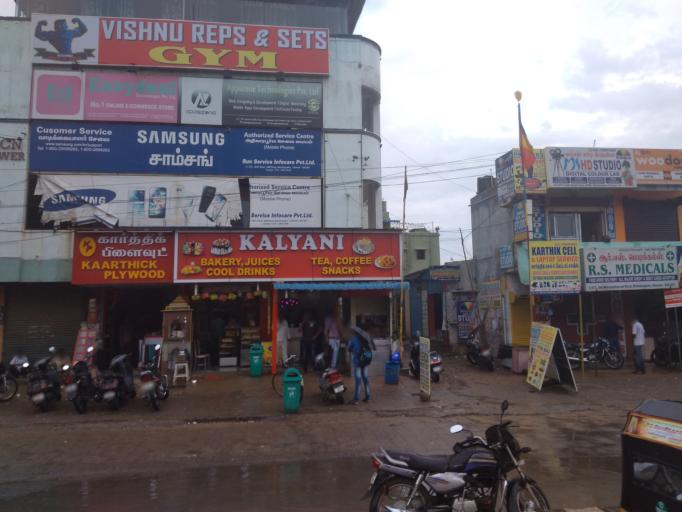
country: IN
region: Tamil Nadu
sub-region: Kancheepuram
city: Perungudi
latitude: 12.9403
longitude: 80.2358
